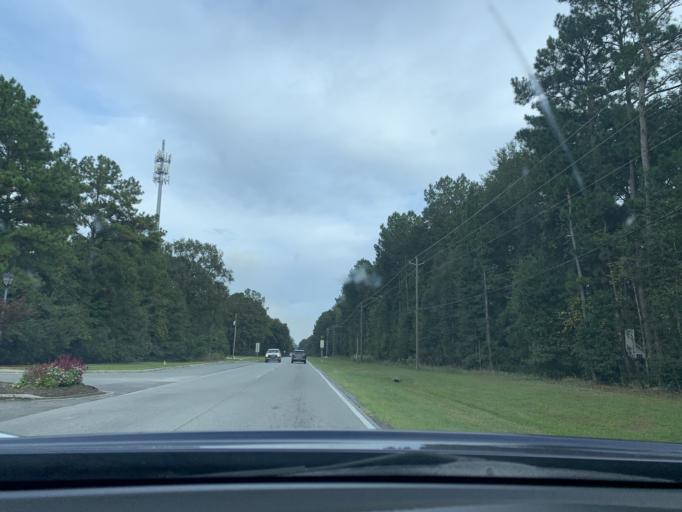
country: US
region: Georgia
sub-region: Chatham County
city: Pooler
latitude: 32.0954
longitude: -81.2674
